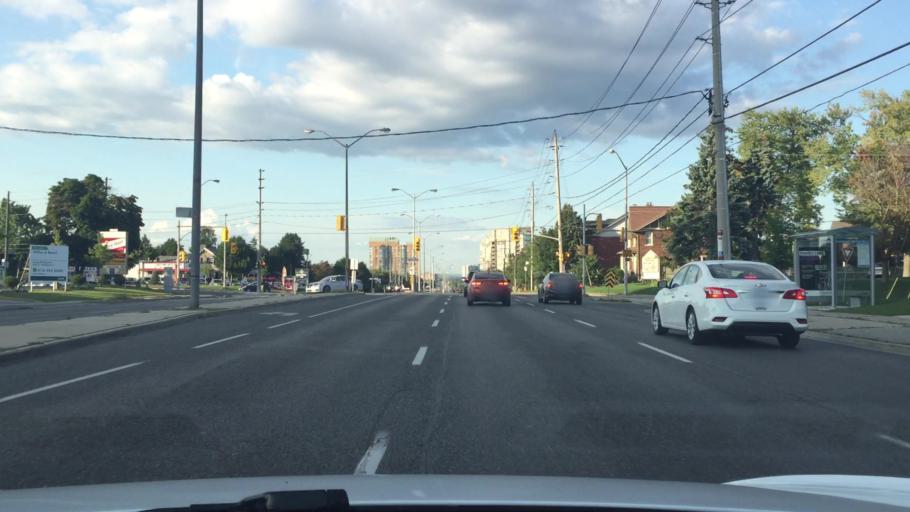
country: CA
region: Ontario
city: Scarborough
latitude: 43.7454
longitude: -79.2098
